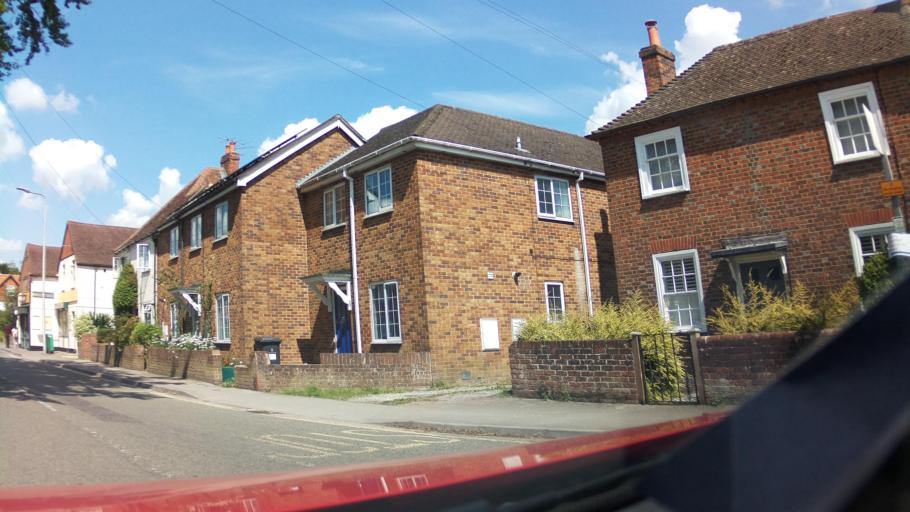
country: GB
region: England
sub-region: West Berkshire
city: Newbury
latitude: 51.4084
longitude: -1.3148
